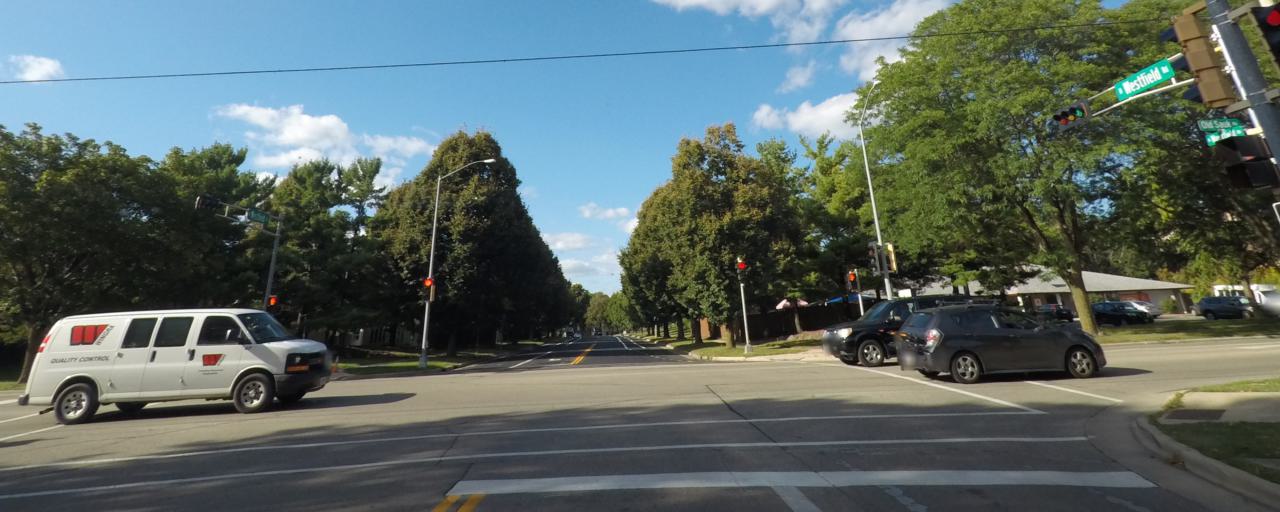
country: US
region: Wisconsin
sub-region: Dane County
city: Middleton
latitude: 43.0749
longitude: -89.5075
